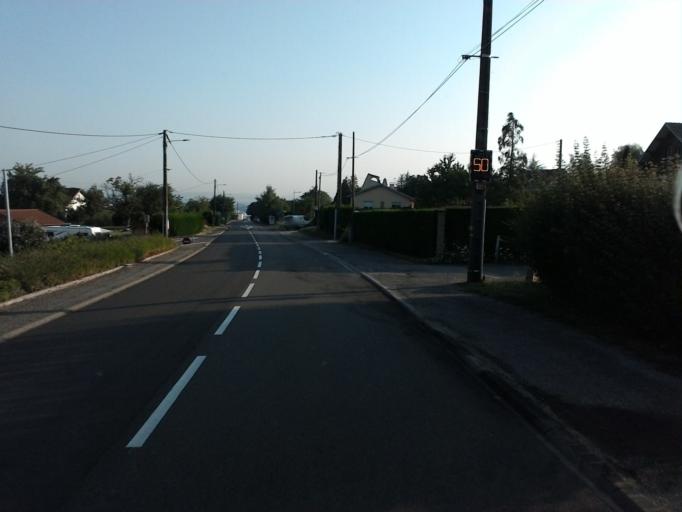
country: FR
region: Franche-Comte
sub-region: Departement de la Haute-Saone
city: Echenoz-la-Meline
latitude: 47.6004
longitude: 6.1413
